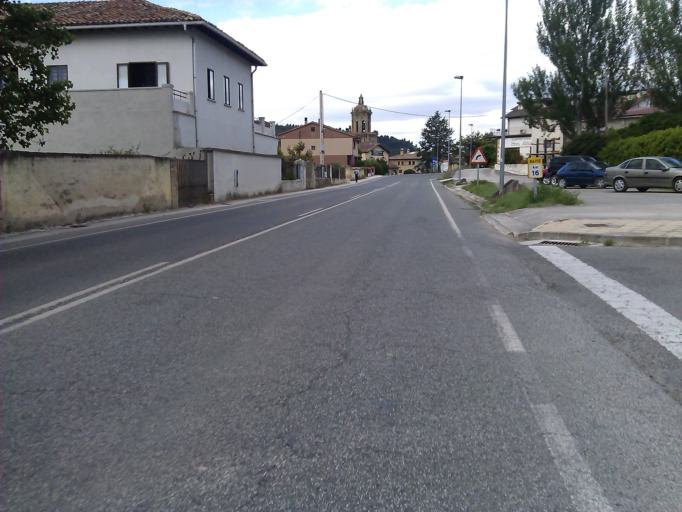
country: ES
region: Navarre
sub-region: Provincia de Navarra
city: Puente la Reina
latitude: 42.6746
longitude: -1.8091
